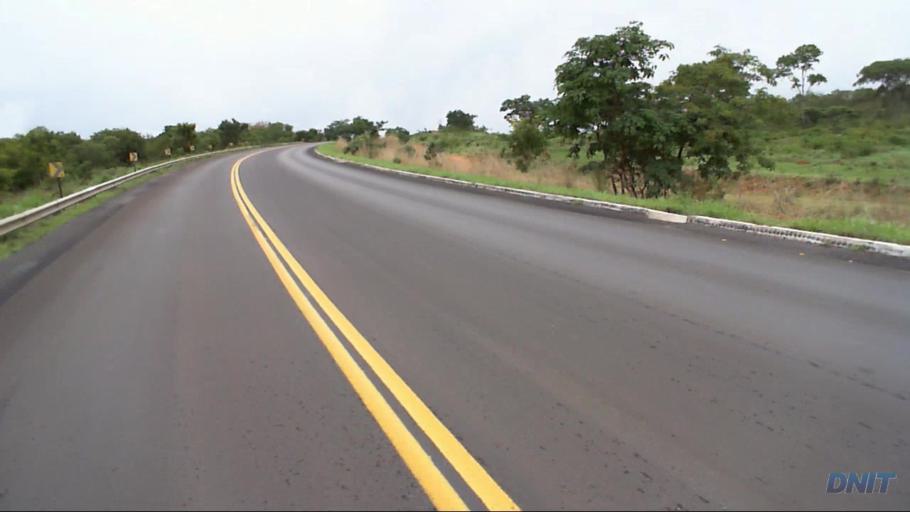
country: BR
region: Goias
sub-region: Padre Bernardo
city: Padre Bernardo
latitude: -15.1936
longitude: -48.4388
